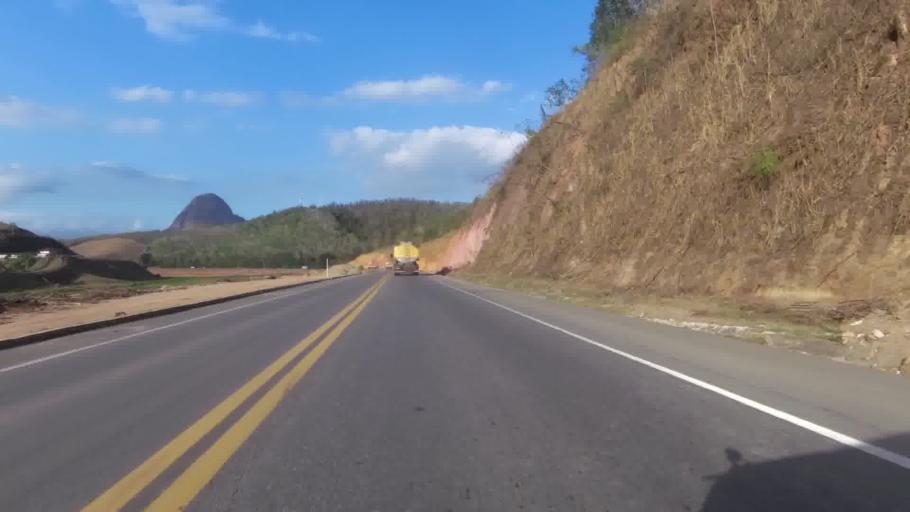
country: BR
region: Espirito Santo
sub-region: Cachoeiro De Itapemirim
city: Cachoeiro de Itapemirim
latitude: -20.8966
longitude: -41.0457
